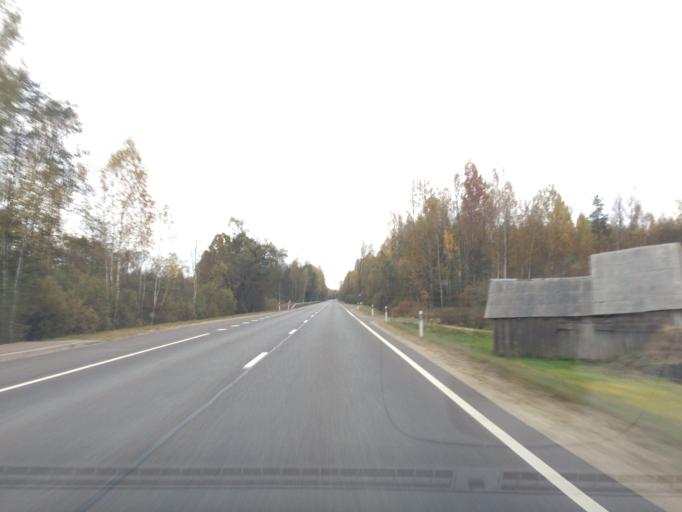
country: LV
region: Livani
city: Livani
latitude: 56.5433
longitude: 26.1229
